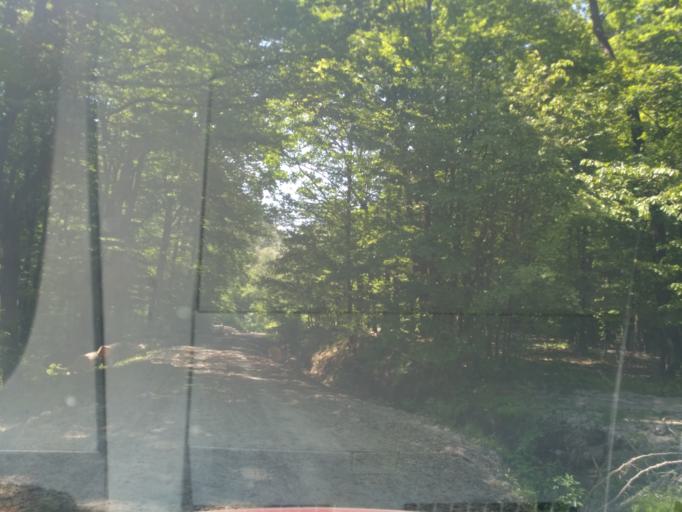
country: SK
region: Presovsky
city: Vranov nad Topl'ou
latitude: 48.8392
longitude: 21.4702
